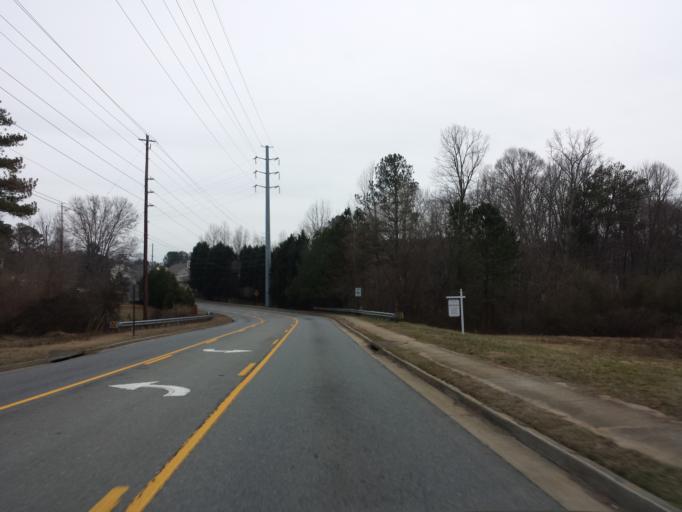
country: US
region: Georgia
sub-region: Cobb County
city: Marietta
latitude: 34.0145
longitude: -84.4829
